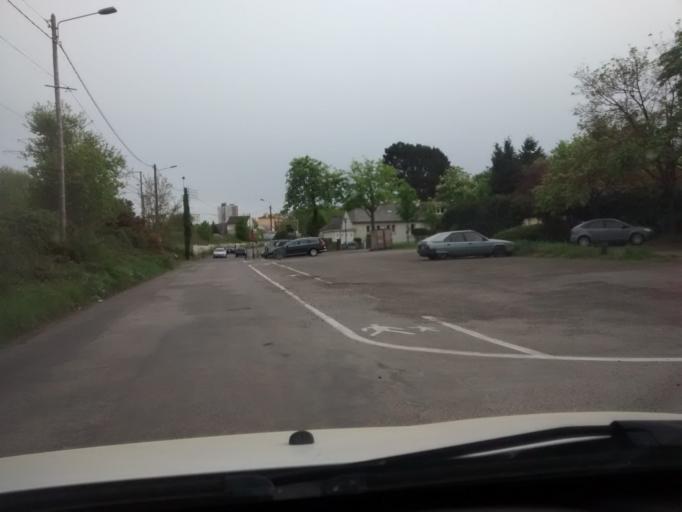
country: FR
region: Brittany
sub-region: Departement d'Ille-et-Vilaine
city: Rennes
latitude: 48.1236
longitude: -1.6887
